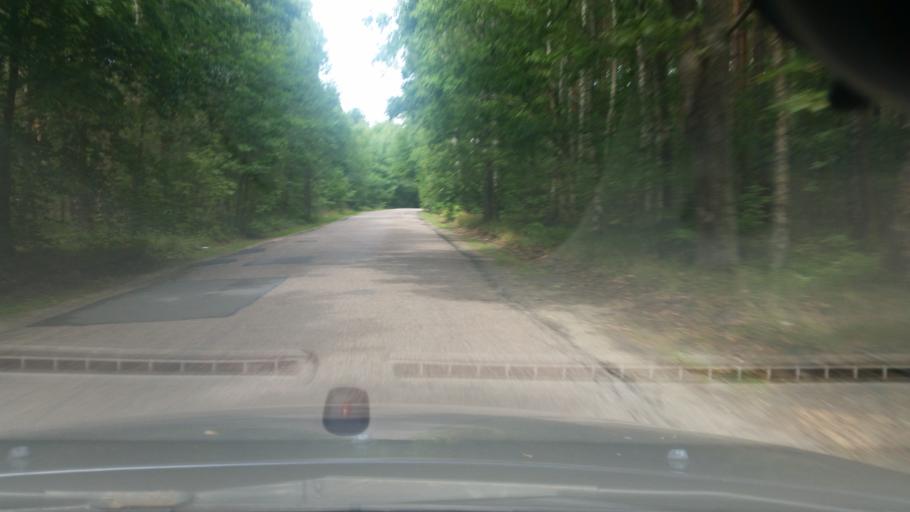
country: PL
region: Pomeranian Voivodeship
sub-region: Powiat wejherowski
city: Choczewo
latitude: 54.7604
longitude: 17.7728
